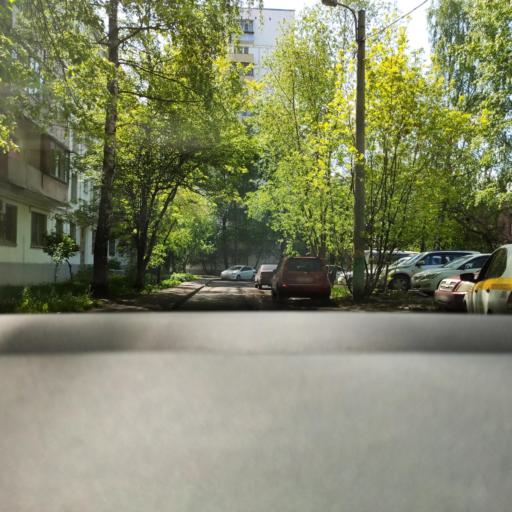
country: RU
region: Moscow
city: Altuf'yevskiy
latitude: 55.8767
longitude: 37.5713
